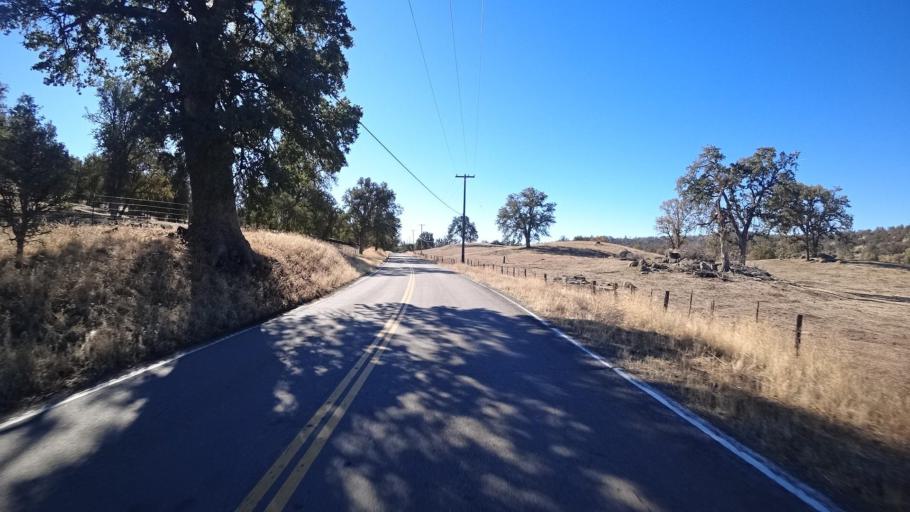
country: US
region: California
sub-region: Kern County
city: Alta Sierra
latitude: 35.7336
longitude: -118.7219
